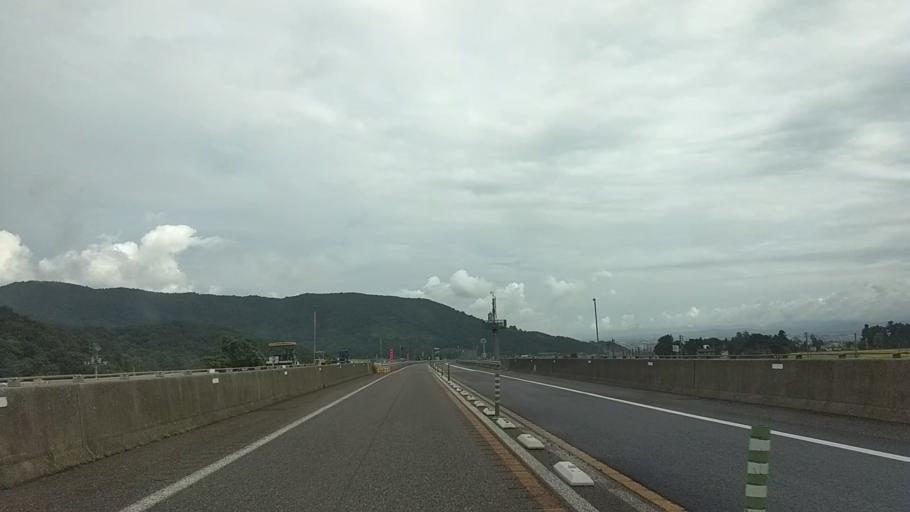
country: JP
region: Niigata
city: Arai
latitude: 37.0143
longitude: 138.2145
